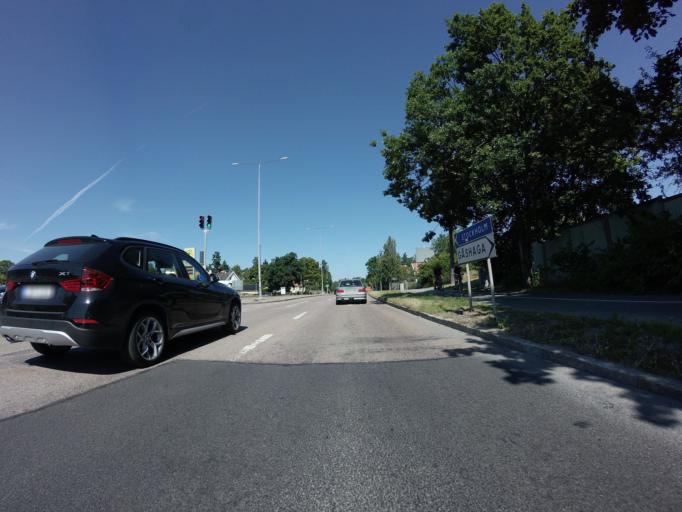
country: SE
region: Stockholm
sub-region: Lidingo
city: Lidingoe
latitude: 59.3566
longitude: 18.1366
